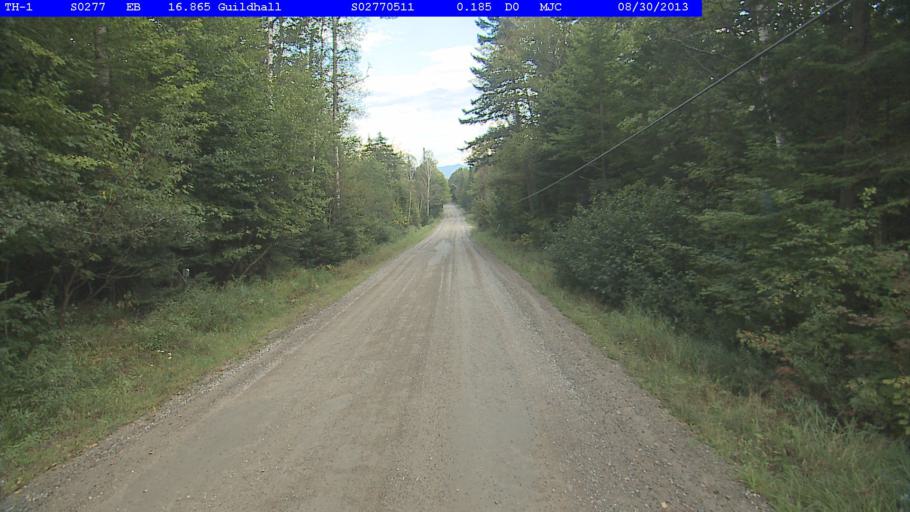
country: US
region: Vermont
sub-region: Essex County
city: Guildhall
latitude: 44.5738
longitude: -71.6661
